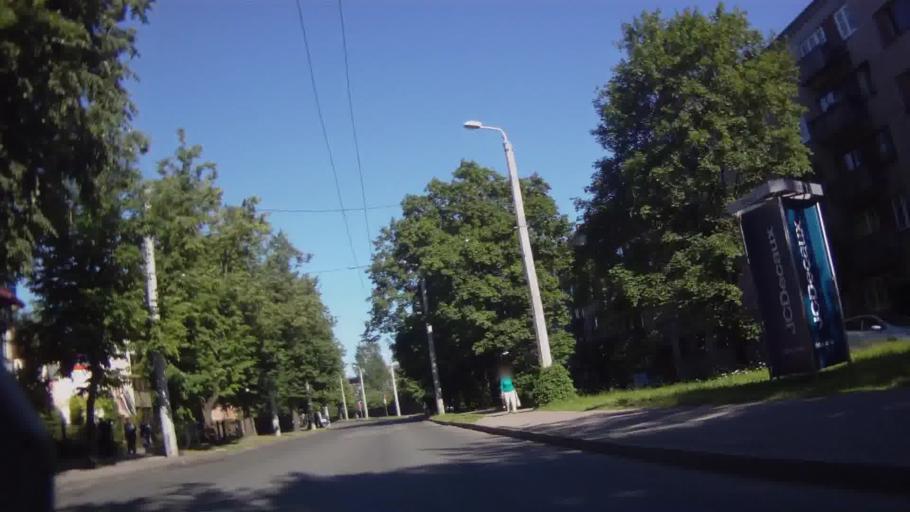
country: LV
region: Riga
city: Riga
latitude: 56.9161
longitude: 24.0919
